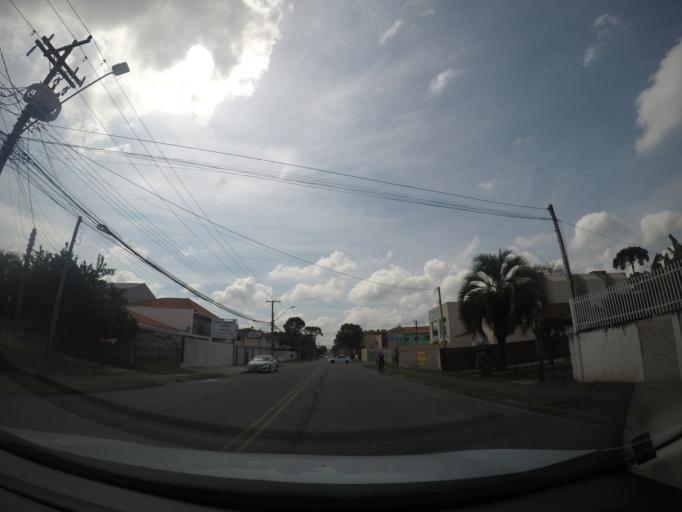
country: BR
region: Parana
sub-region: Curitiba
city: Curitiba
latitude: -25.4756
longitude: -49.2644
